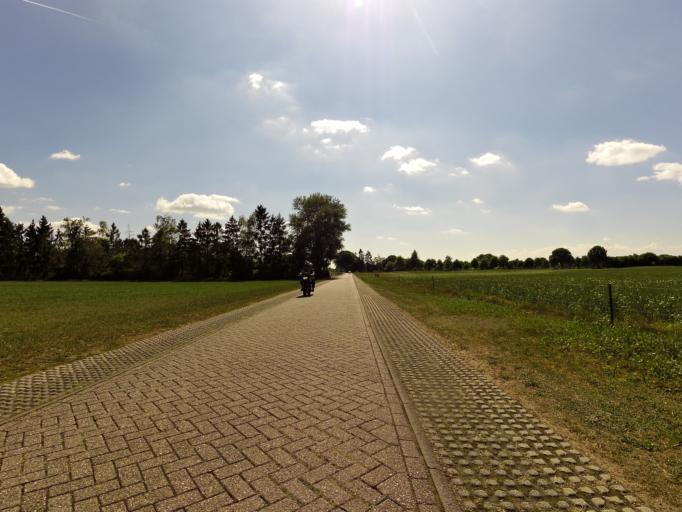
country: NL
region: Gelderland
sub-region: Gemeente Bronckhorst
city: Zelhem
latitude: 52.0331
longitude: 6.3515
